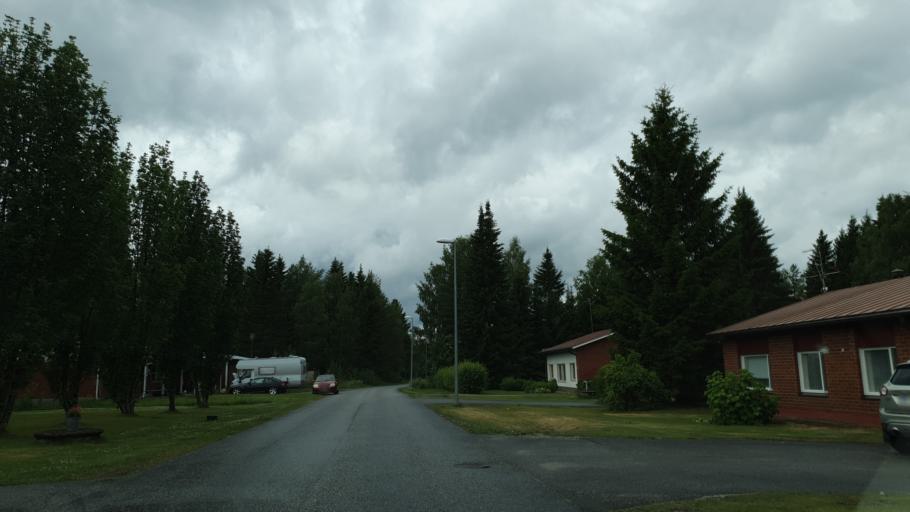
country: FI
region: Kainuu
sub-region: Kehys-Kainuu
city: Kuhmo
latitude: 64.1184
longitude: 29.5132
